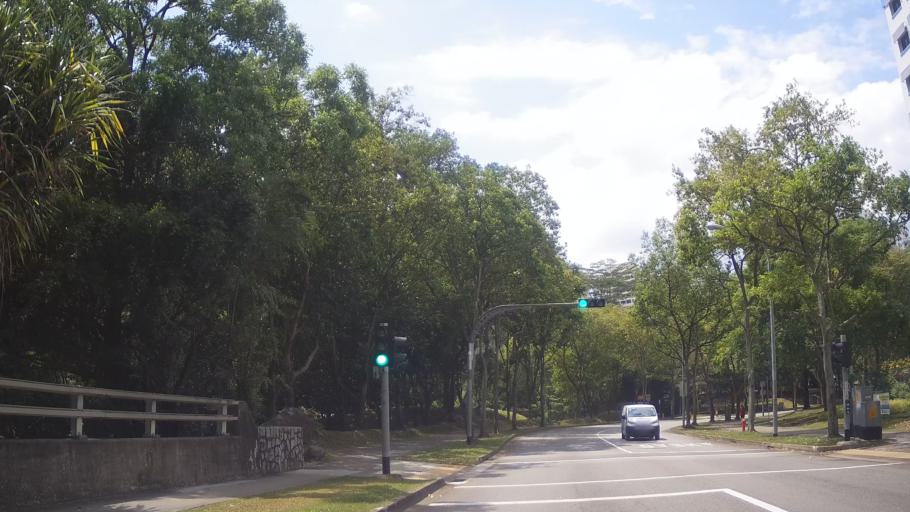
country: MY
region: Johor
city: Johor Bahru
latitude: 1.3823
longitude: 103.7670
